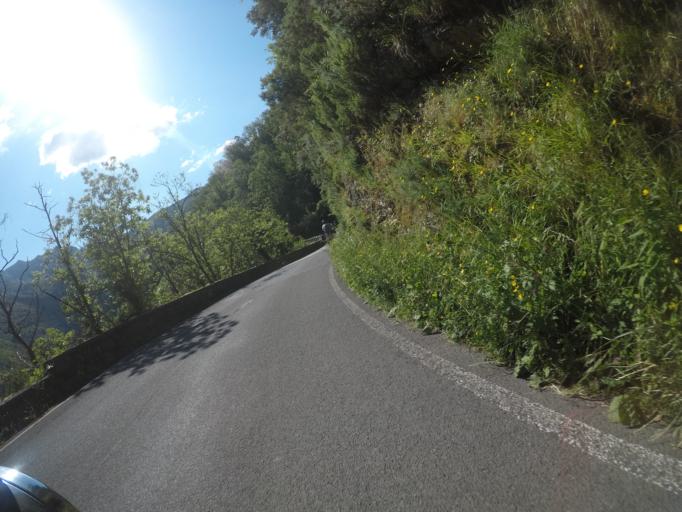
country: IT
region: Tuscany
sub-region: Provincia di Massa-Carrara
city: Montignoso
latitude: 44.0530
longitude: 10.1773
